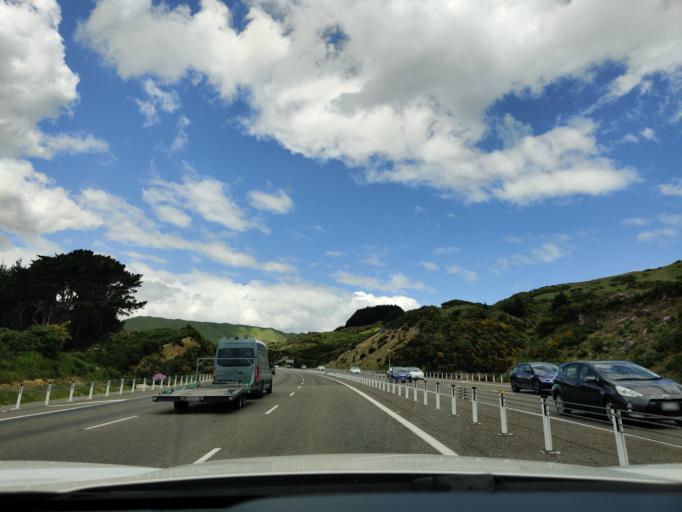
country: NZ
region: Wellington
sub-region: Porirua City
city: Porirua
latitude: -41.1520
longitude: 174.8578
